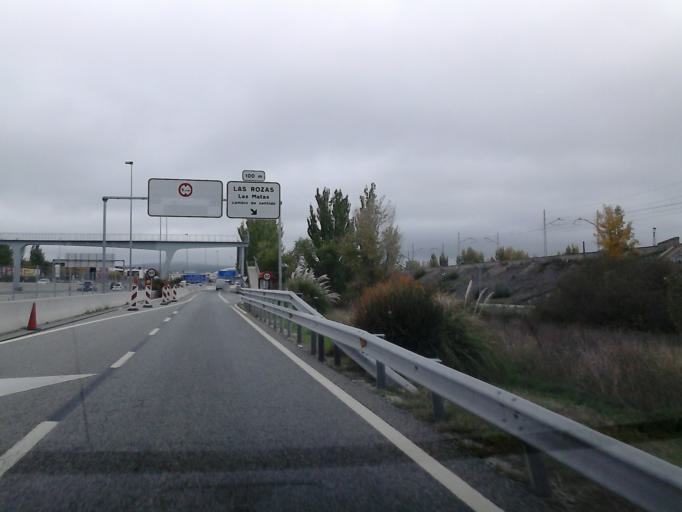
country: ES
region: Madrid
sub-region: Provincia de Madrid
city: Las Matas
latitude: 40.5406
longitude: -3.8917
